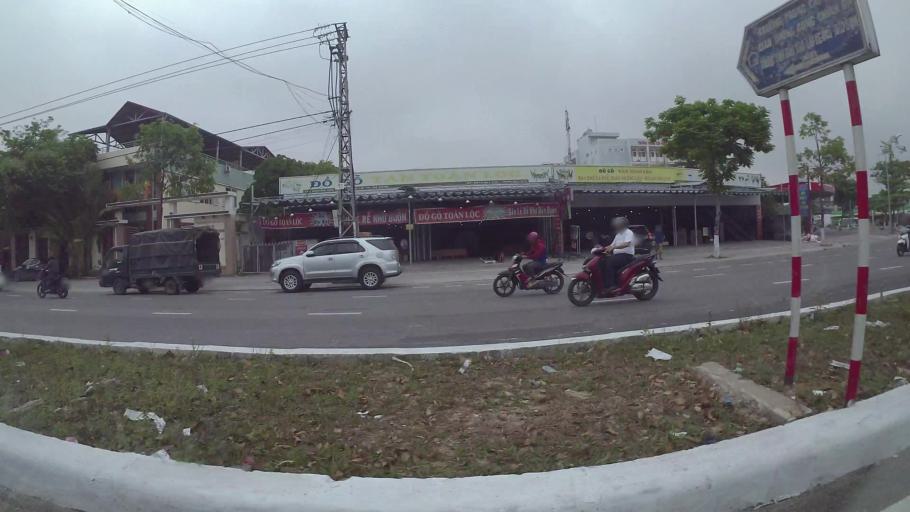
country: VN
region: Da Nang
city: Cam Le
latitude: 16.0255
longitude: 108.2089
